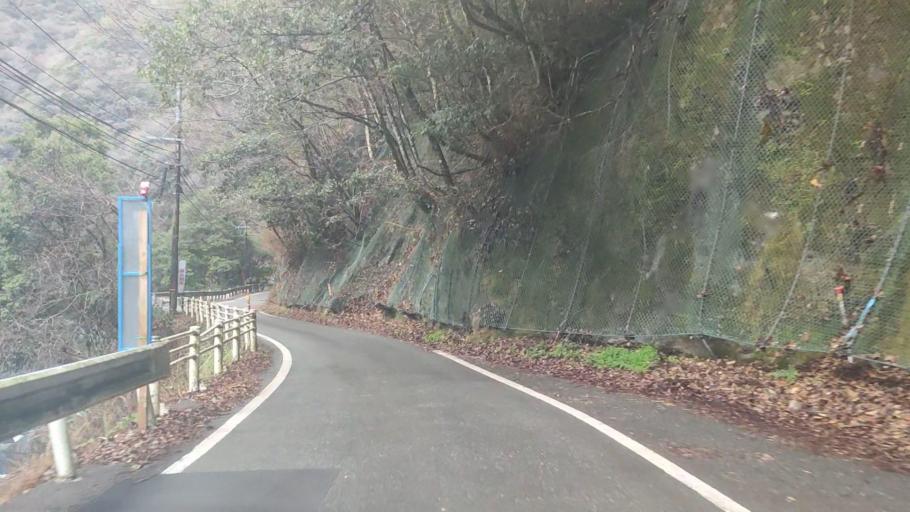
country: JP
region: Kumamoto
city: Matsubase
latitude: 32.4837
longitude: 130.8917
